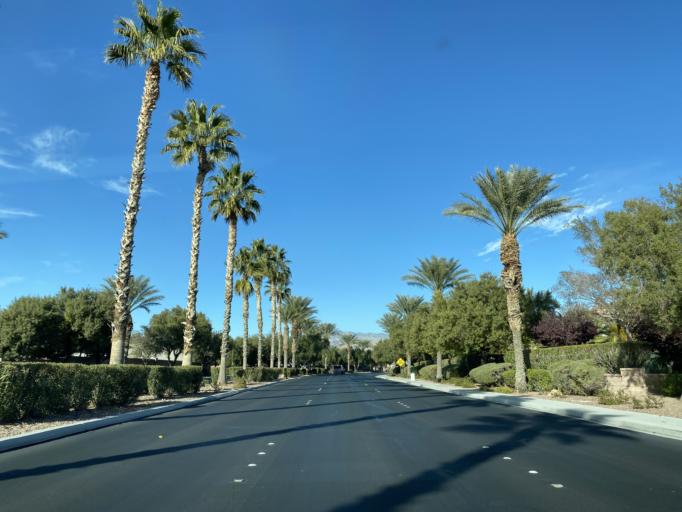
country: US
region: Nevada
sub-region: Clark County
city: North Las Vegas
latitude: 36.3105
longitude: -115.2601
